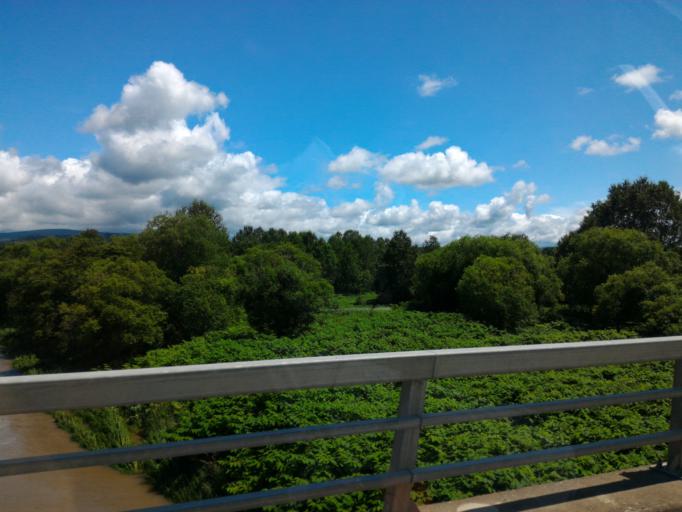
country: JP
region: Hokkaido
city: Nayoro
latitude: 44.5259
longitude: 142.3257
